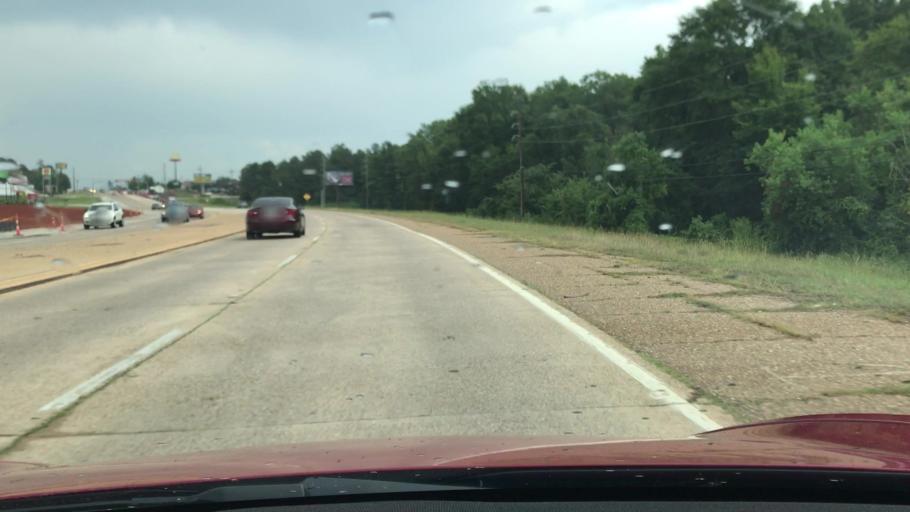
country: US
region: Louisiana
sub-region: Bossier Parish
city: Bossier City
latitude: 32.3985
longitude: -93.7684
